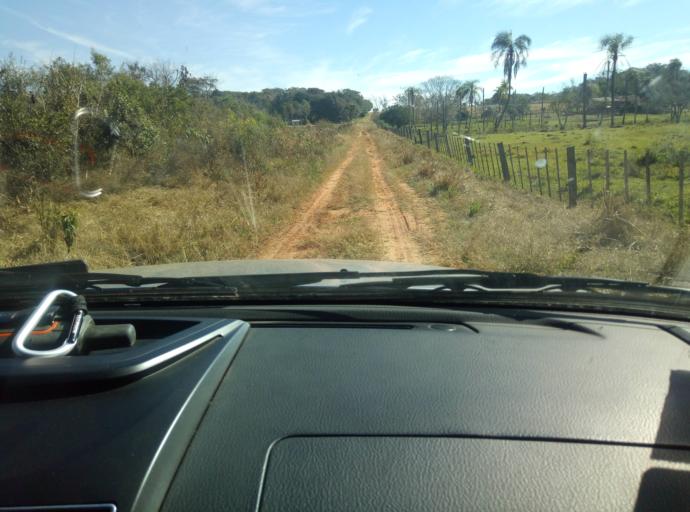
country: PY
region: Caaguazu
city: Carayao
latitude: -25.1750
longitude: -56.3111
